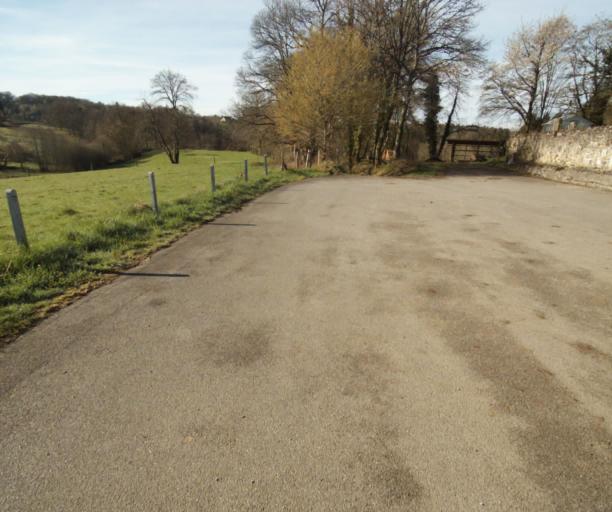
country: FR
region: Limousin
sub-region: Departement de la Correze
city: Laguenne
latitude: 45.2646
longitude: 1.8703
